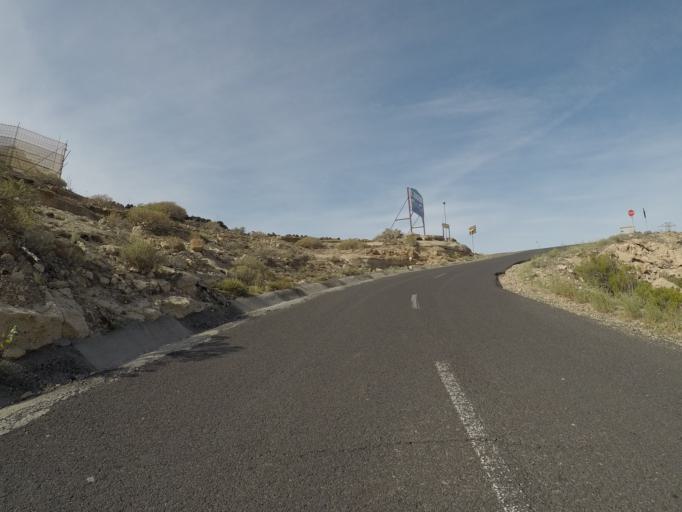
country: ES
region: Canary Islands
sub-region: Provincia de Santa Cruz de Tenerife
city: Lomo de Arico
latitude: 28.1167
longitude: -16.4743
